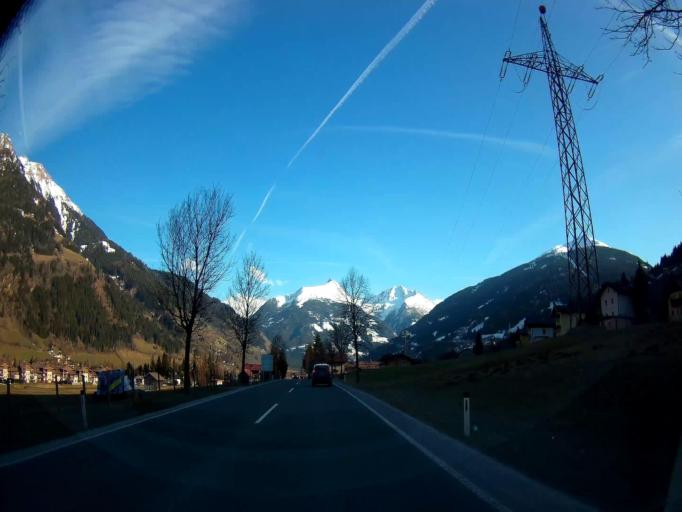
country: AT
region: Salzburg
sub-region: Politischer Bezirk Sankt Johann im Pongau
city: Bad Hofgastein
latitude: 47.1618
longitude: 13.1017
